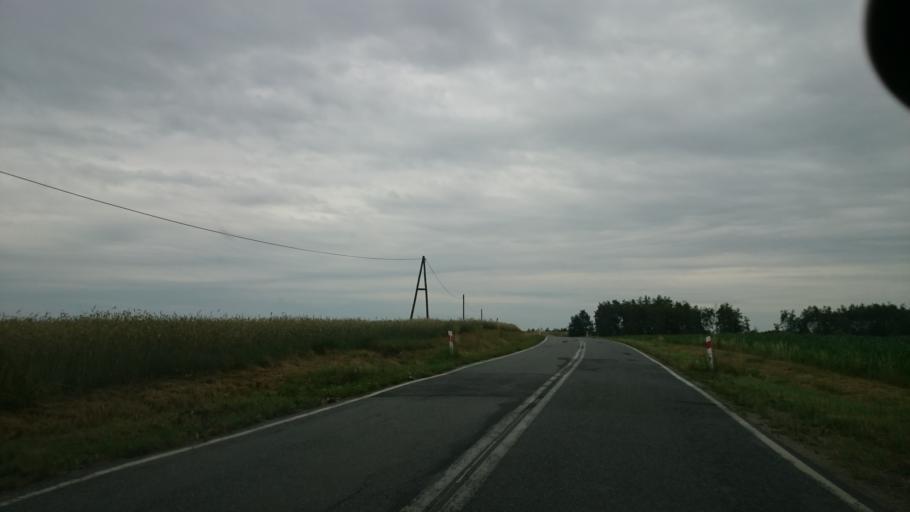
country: PL
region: Lower Silesian Voivodeship
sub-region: Powiat strzelinski
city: Przeworno
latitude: 50.6431
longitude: 17.1811
